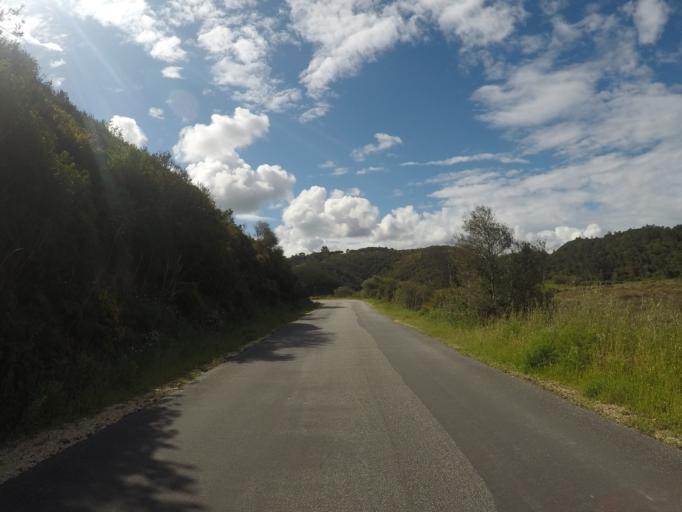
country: PT
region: Beja
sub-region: Odemira
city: Sao Teotonio
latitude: 37.4365
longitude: -8.7870
